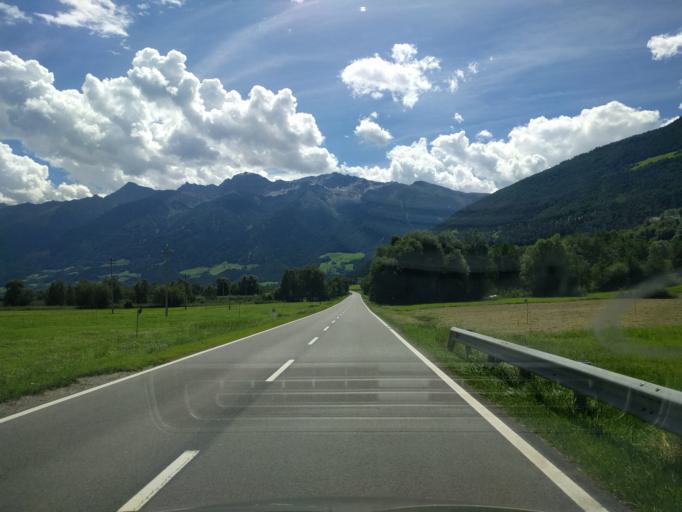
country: IT
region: Trentino-Alto Adige
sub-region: Bolzano
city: Sluderno
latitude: 46.6448
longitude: 10.5688
